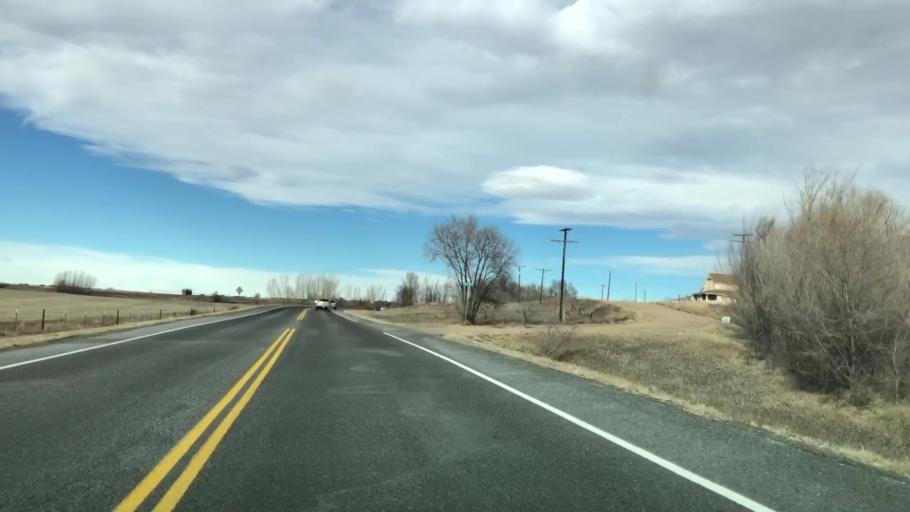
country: US
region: Colorado
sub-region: Weld County
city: Windsor
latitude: 40.5097
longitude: -104.9268
